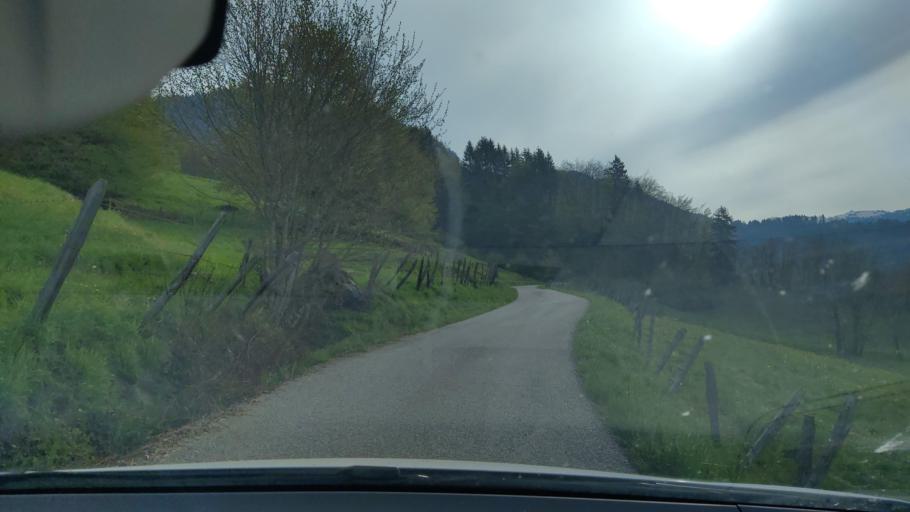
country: FR
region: Rhone-Alpes
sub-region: Departement de la Savoie
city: Ugine
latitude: 45.7713
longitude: 6.4106
